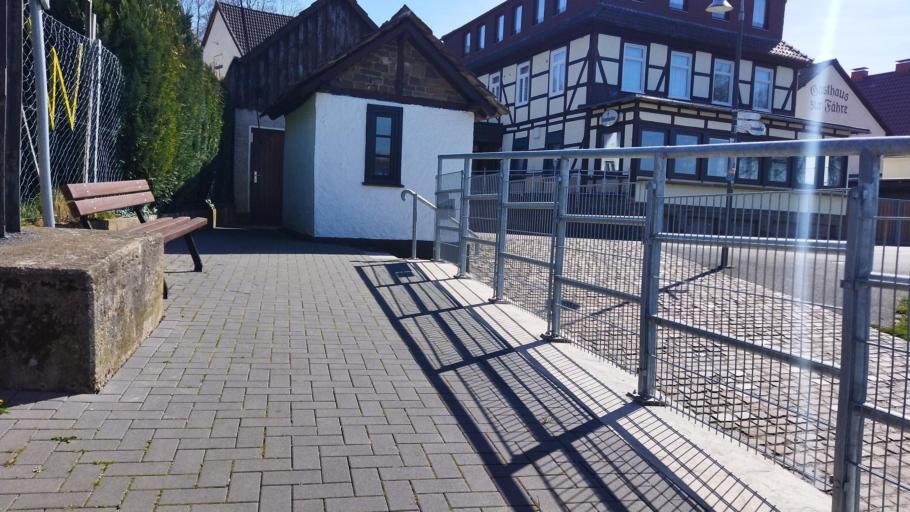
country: DE
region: Lower Saxony
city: Bad Karlshafen
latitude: 51.6434
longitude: 9.4187
